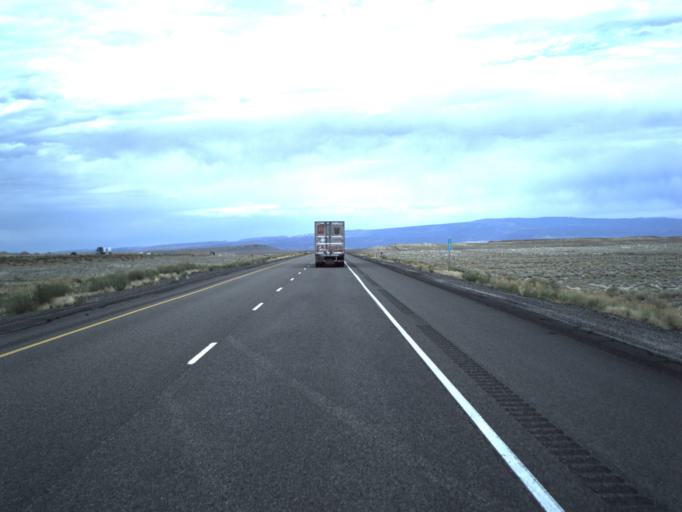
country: US
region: Utah
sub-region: Grand County
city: Moab
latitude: 38.9418
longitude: -109.5501
